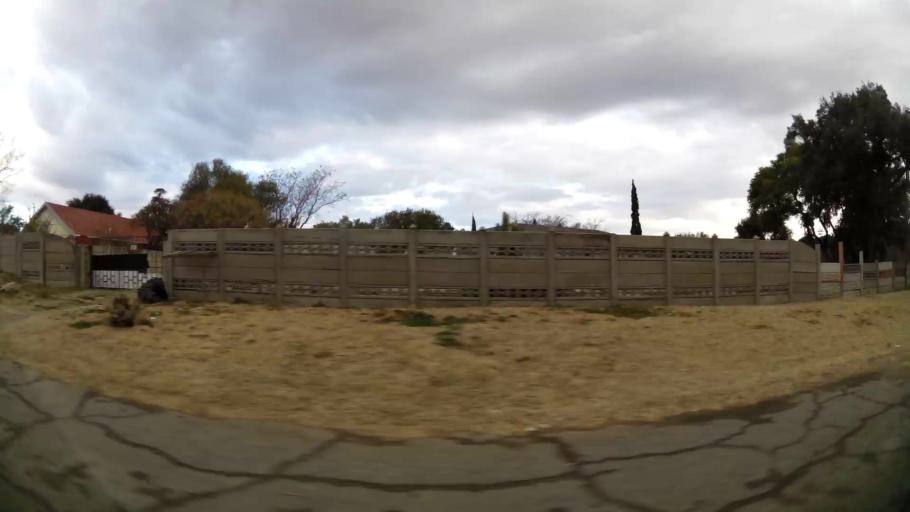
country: ZA
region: Orange Free State
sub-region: Lejweleputswa District Municipality
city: Welkom
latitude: -27.9671
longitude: 26.7204
